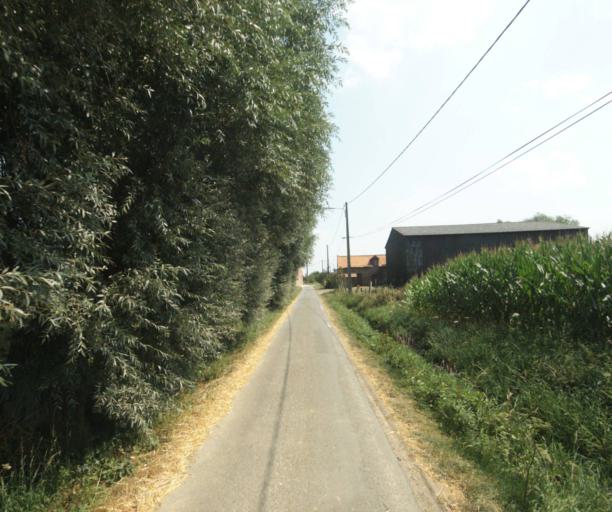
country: FR
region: Nord-Pas-de-Calais
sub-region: Departement du Nord
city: Quesnoy-sur-Deule
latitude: 50.7286
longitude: 3.0319
